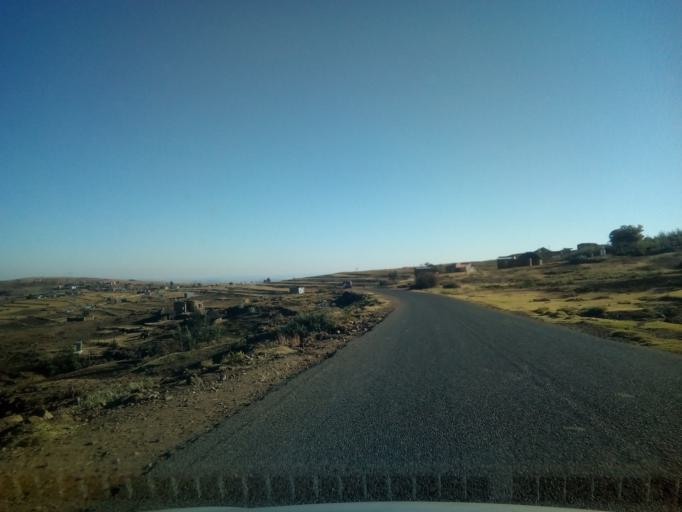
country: LS
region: Berea
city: Teyateyaneng
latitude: -29.2586
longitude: 27.8040
